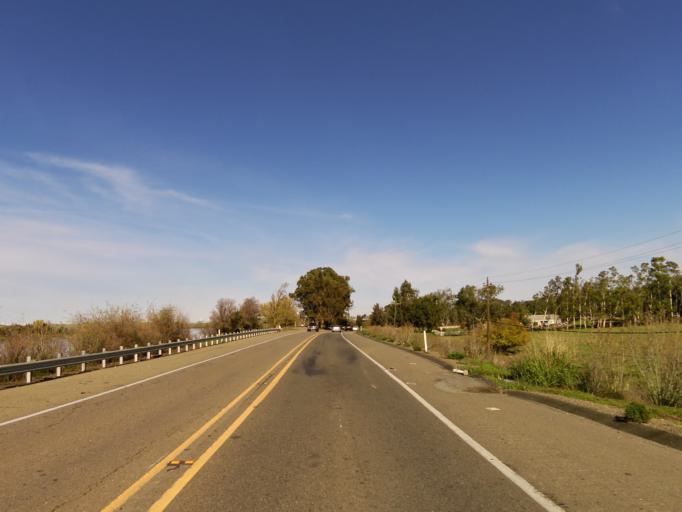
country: US
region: California
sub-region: Solano County
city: Rio Vista
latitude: 38.0966
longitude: -121.7062
